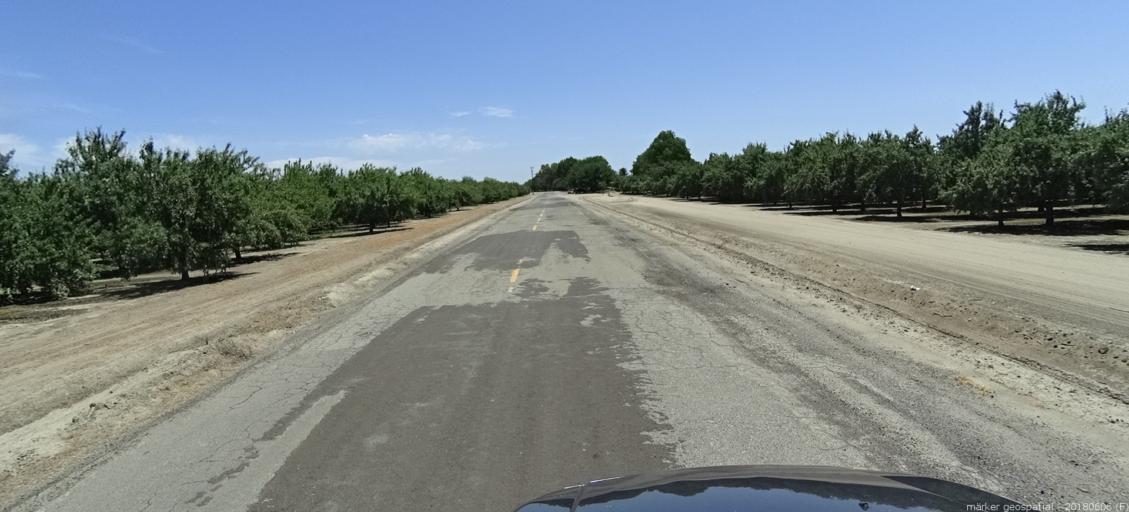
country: US
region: California
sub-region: Fresno County
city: Mendota
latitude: 36.8071
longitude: -120.3553
